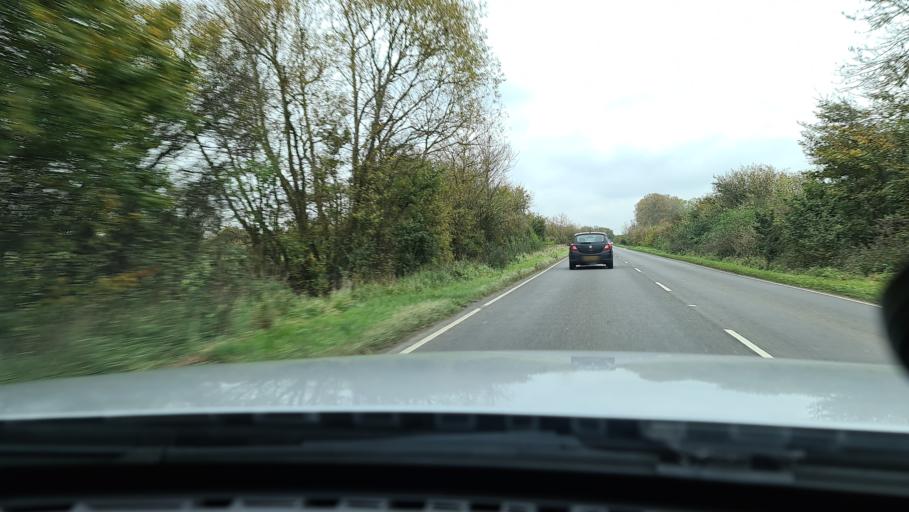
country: GB
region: England
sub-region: Oxfordshire
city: Bicester
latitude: 51.8761
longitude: -1.0853
